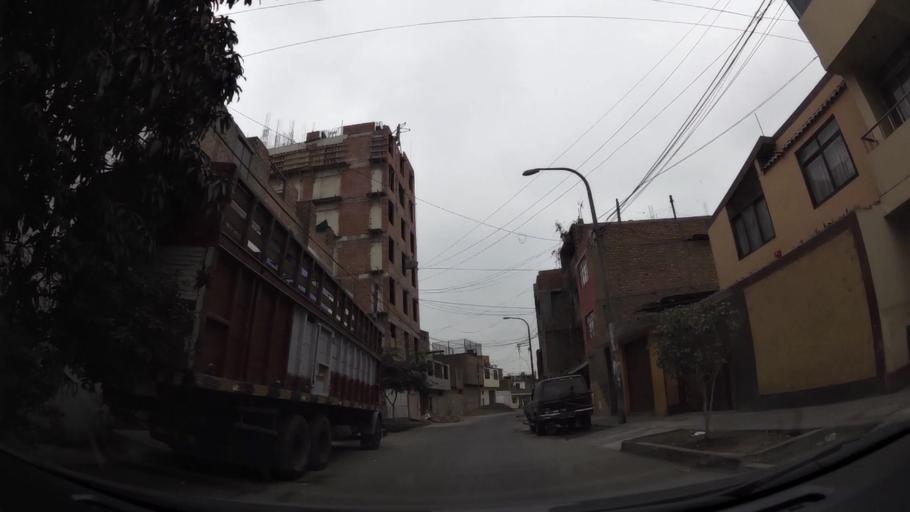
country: PE
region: Lima
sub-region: Lima
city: Independencia
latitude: -11.9721
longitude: -77.0581
